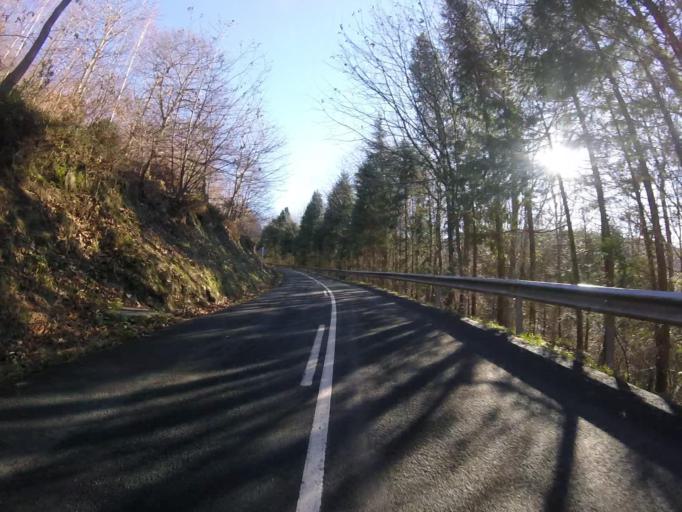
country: ES
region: Basque Country
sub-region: Provincia de Guipuzcoa
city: Irun
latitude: 43.3150
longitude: -1.7611
